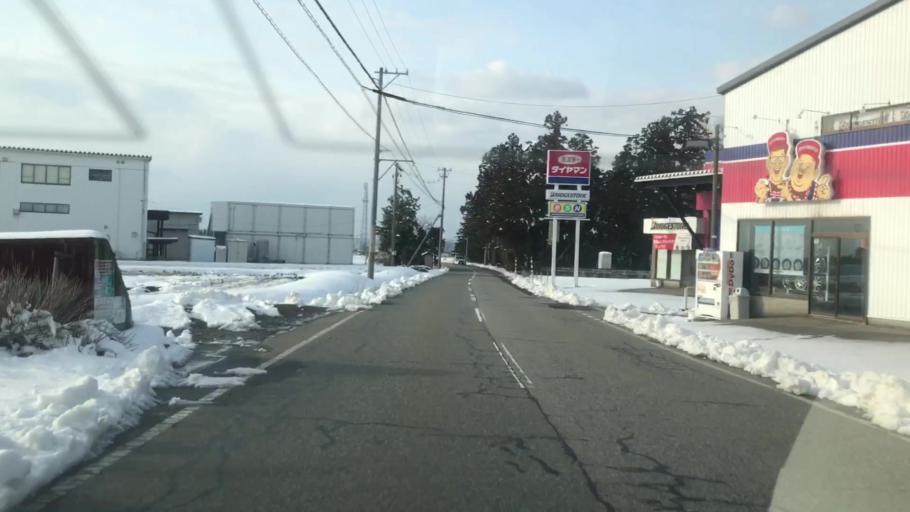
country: JP
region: Toyama
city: Toyama-shi
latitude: 36.6374
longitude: 137.2631
